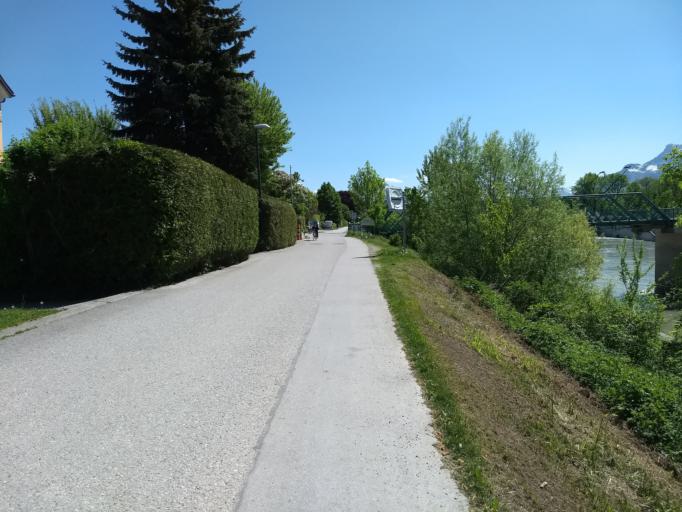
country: AT
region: Salzburg
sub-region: Politischer Bezirk Salzburg-Umgebung
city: Bergheim
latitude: 47.8240
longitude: 13.0336
